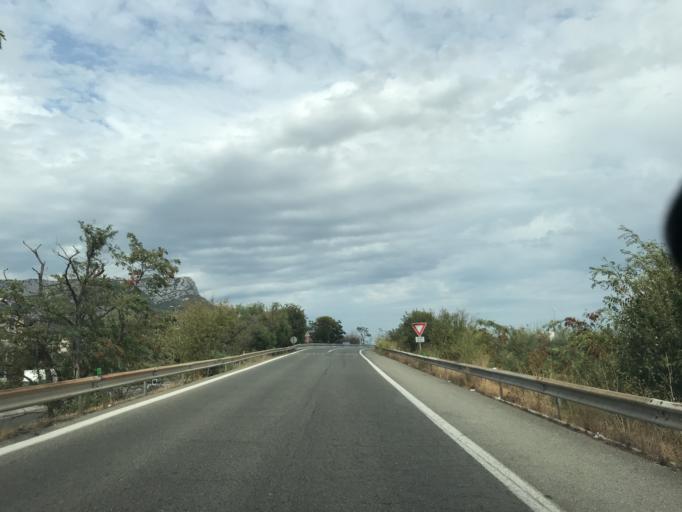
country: FR
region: Provence-Alpes-Cote d'Azur
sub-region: Departement du Var
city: La Valette-du-Var
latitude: 43.1308
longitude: 5.9799
